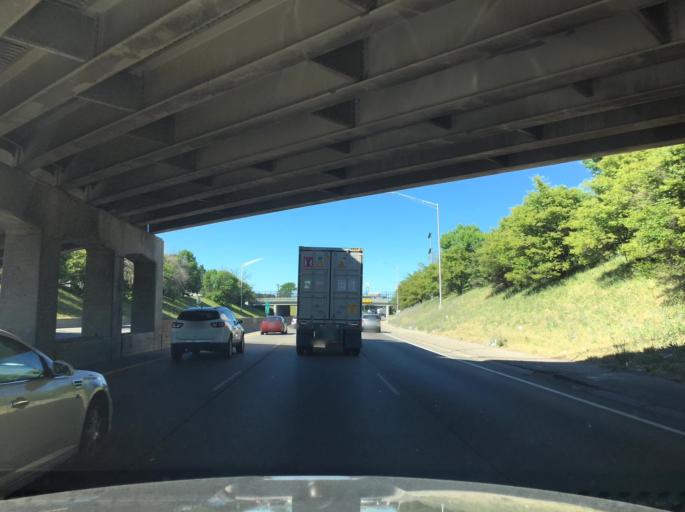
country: US
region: Michigan
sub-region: Wayne County
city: Harper Woods
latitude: 42.4206
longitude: -82.9321
